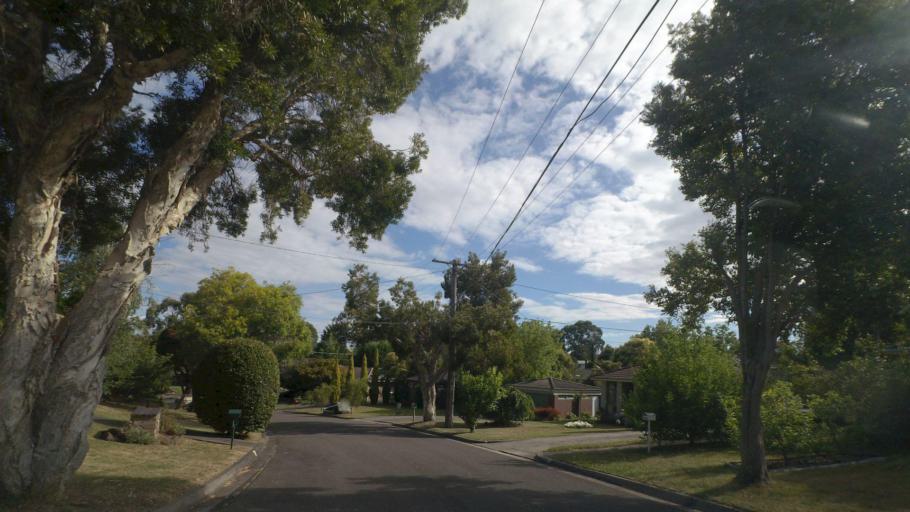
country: AU
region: Victoria
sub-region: Maroondah
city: Warranwood
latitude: -37.7929
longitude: 145.2499
